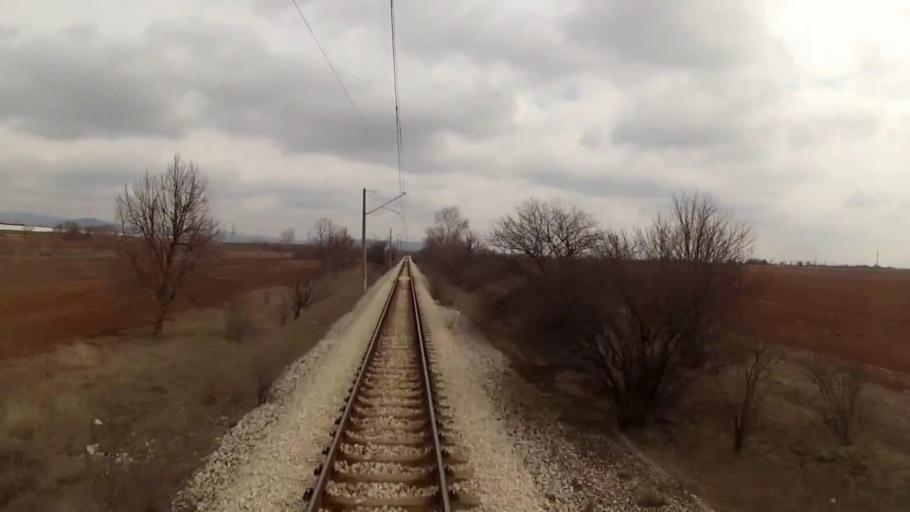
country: BG
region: Sofiya
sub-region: Obshtina Elin Pelin
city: Elin Pelin
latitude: 42.7107
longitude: 23.6074
